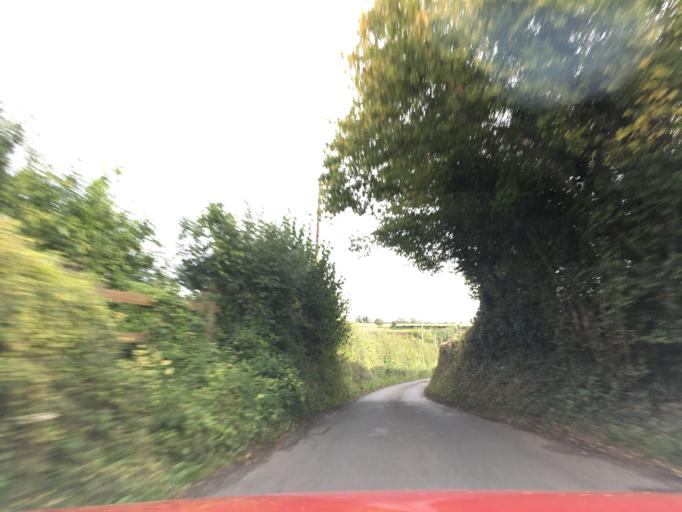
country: GB
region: England
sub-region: South Gloucestershire
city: Alveston
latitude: 51.5985
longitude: -2.5481
